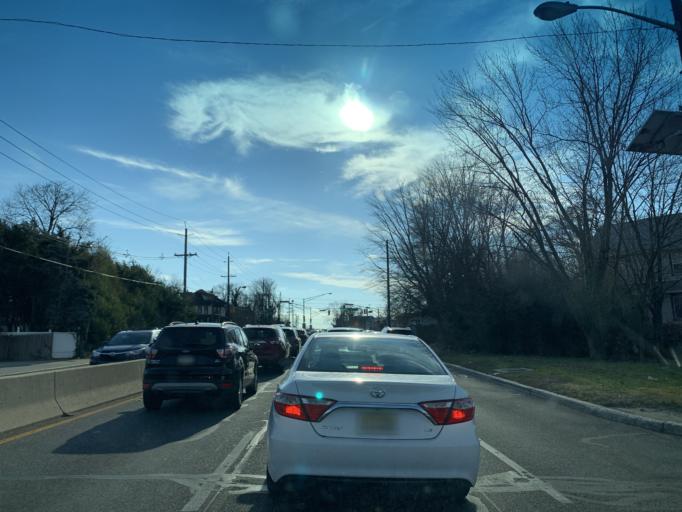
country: US
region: New Jersey
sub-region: Camden County
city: Wood-Lynne
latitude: 39.9083
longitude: -75.0944
